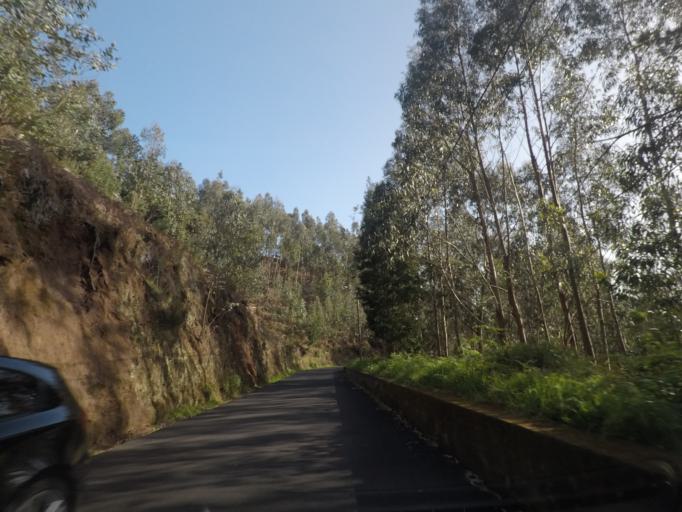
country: PT
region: Madeira
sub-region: Ribeira Brava
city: Campanario
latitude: 32.6723
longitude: -17.0037
